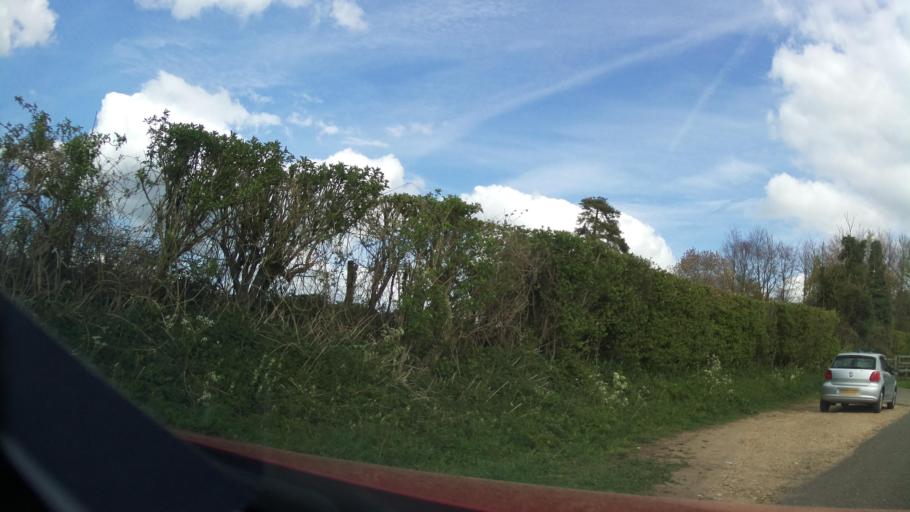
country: GB
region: England
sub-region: Hampshire
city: Romsey
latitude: 51.0380
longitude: -1.5140
